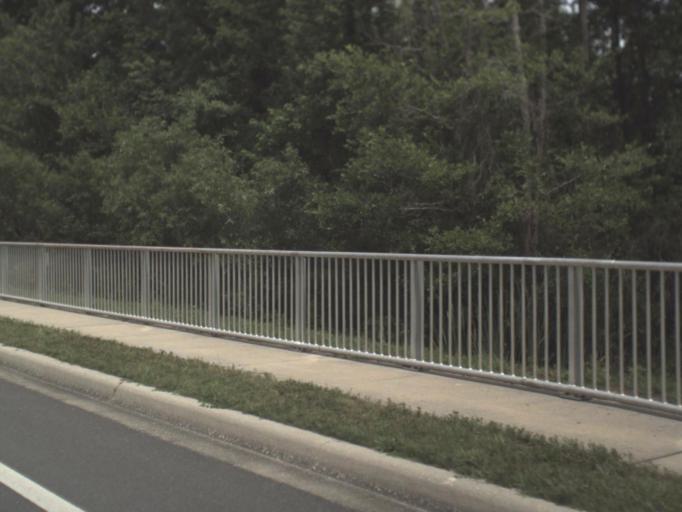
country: US
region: Florida
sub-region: Putnam County
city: Interlachen
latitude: 29.6289
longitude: -81.8288
